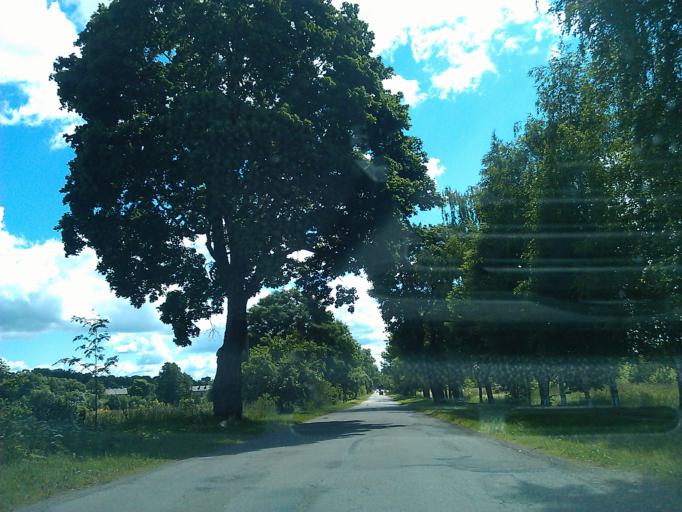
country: LV
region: Varaklani
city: Varaklani
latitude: 56.6073
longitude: 26.7662
